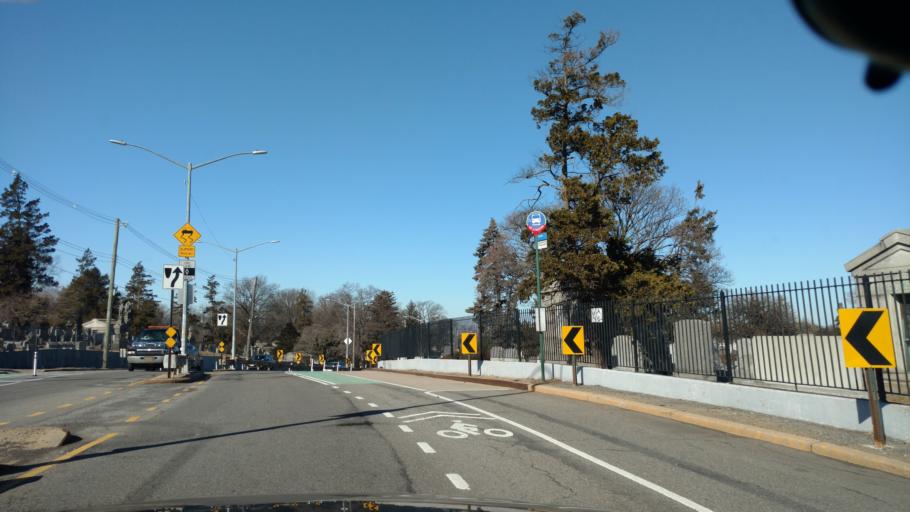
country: US
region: New York
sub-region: Kings County
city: East New York
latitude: 40.6936
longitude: -73.8841
